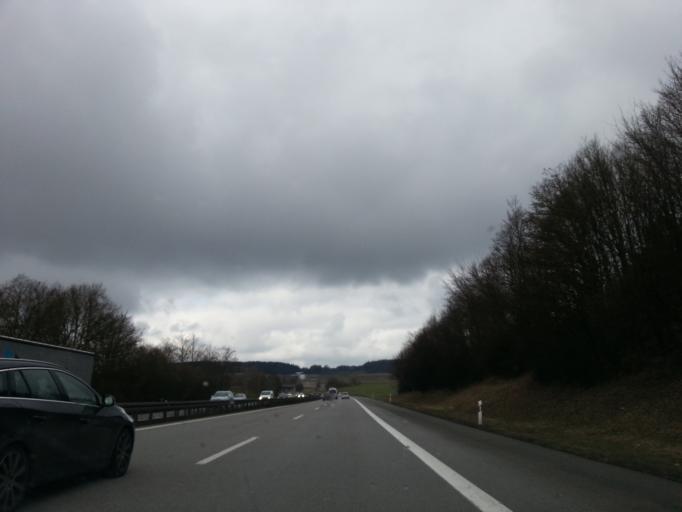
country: DE
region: Bavaria
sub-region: Upper Palatinate
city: Hohenfels
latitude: 49.1563
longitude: 11.8412
